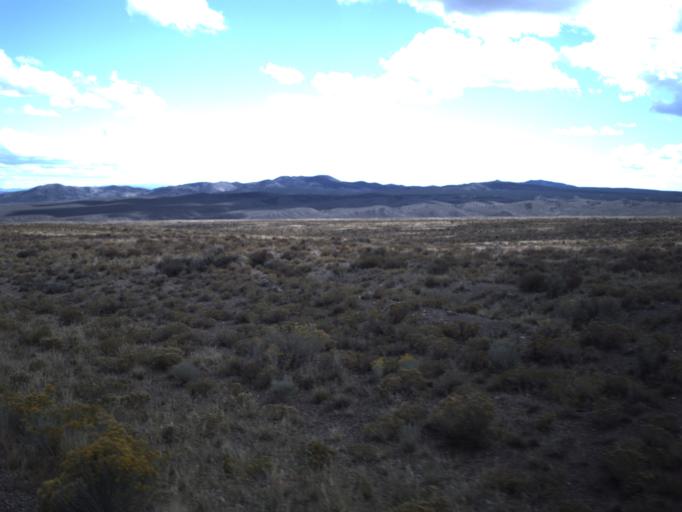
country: US
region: Utah
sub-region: Beaver County
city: Milford
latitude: 38.4530
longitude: -113.2071
